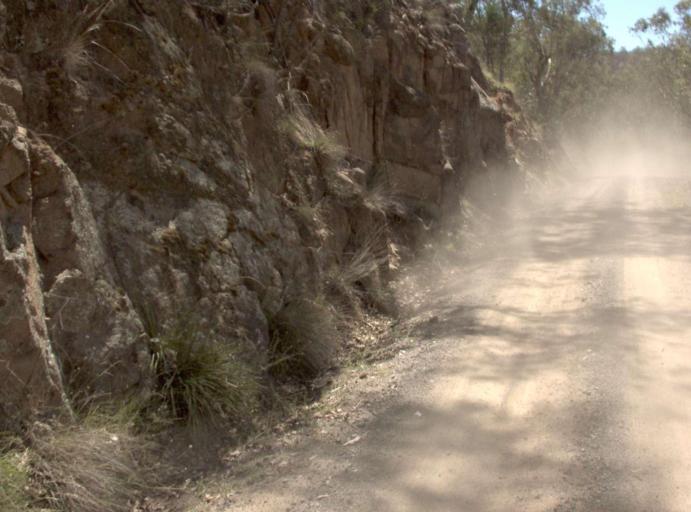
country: AU
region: New South Wales
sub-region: Snowy River
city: Jindabyne
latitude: -37.0790
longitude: 148.4876
